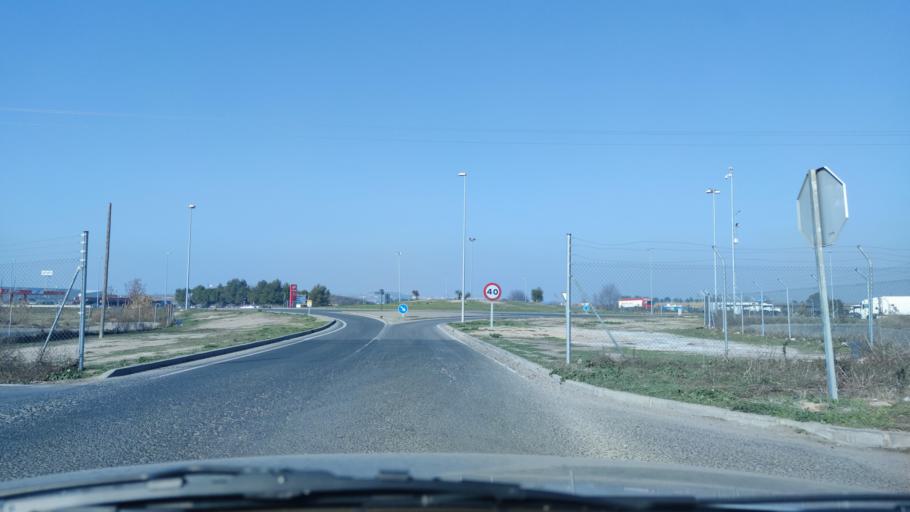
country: ES
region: Catalonia
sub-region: Provincia de Lleida
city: Alcoletge
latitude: 41.6251
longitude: 0.7212
